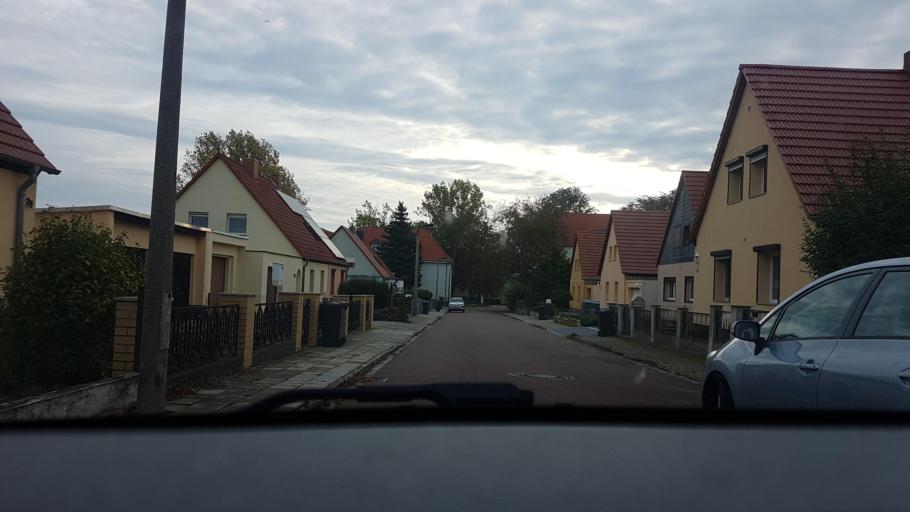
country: DE
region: Saxony-Anhalt
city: Bernburg
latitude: 51.7821
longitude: 11.7614
